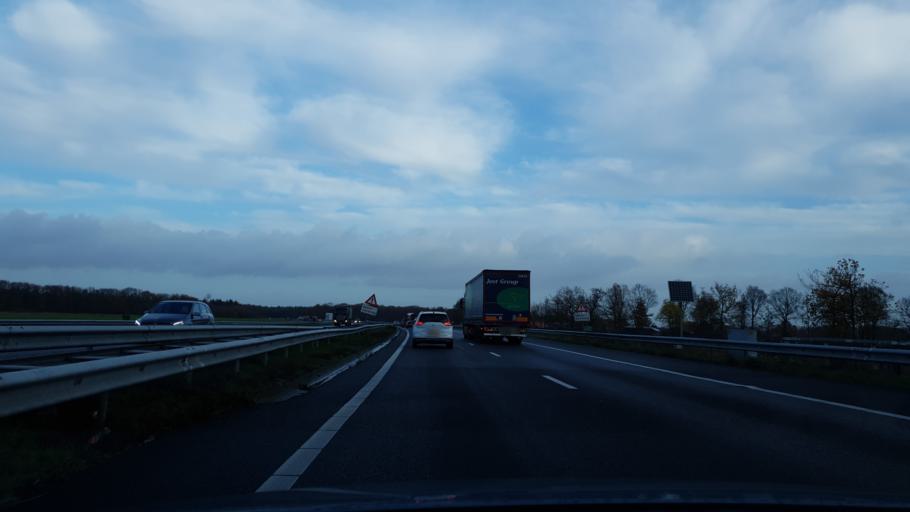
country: NL
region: Limburg
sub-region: Gemeente Venray
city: Venray
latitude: 51.5601
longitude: 5.9937
